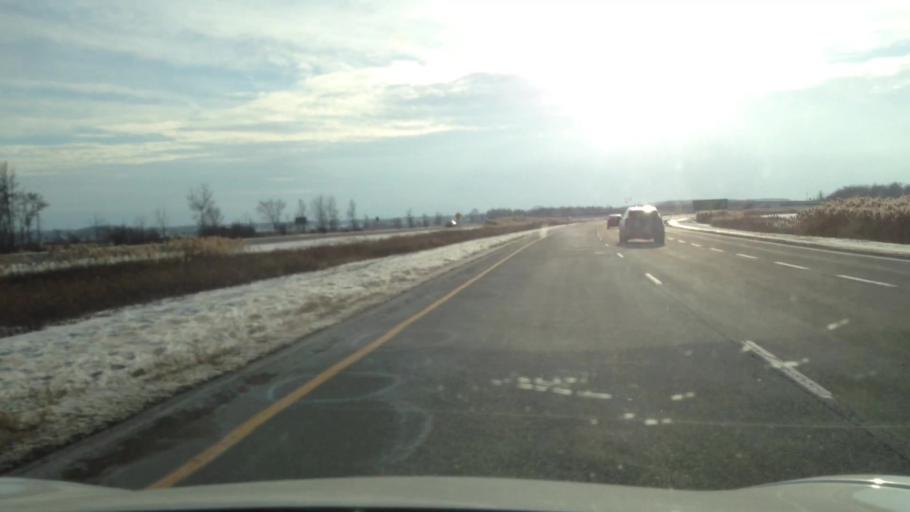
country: CA
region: Ontario
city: Casselman
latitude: 45.3479
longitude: -74.8929
